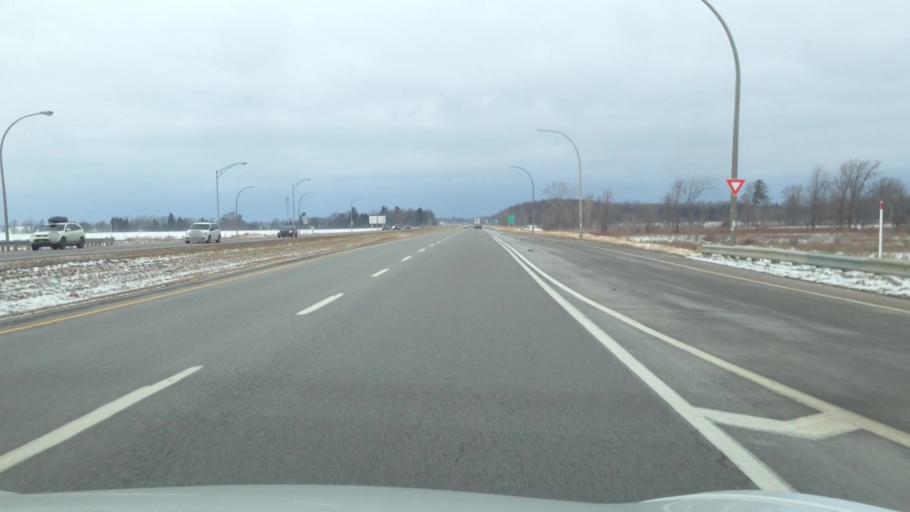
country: CA
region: Quebec
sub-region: Monteregie
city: Rigaud
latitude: 45.4954
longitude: -74.3530
